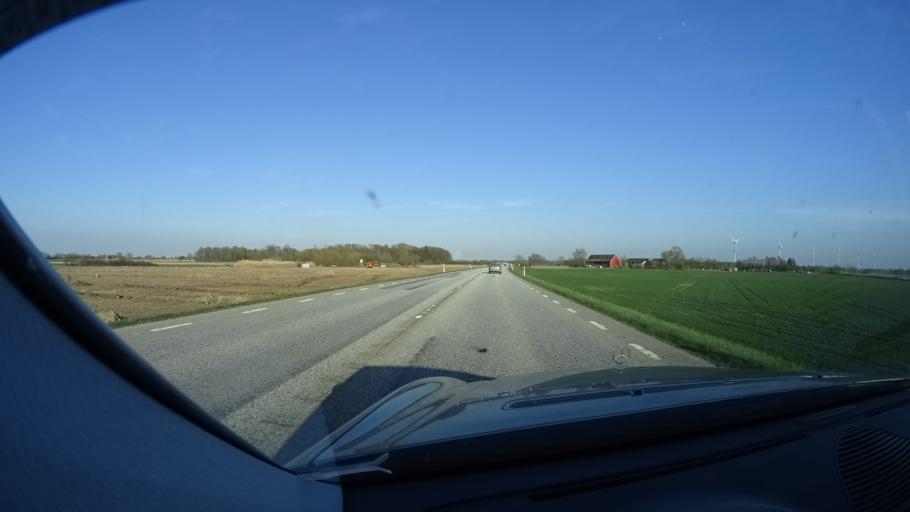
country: SE
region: Skane
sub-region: Eslovs Kommun
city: Stehag
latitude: 55.8504
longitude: 13.4206
